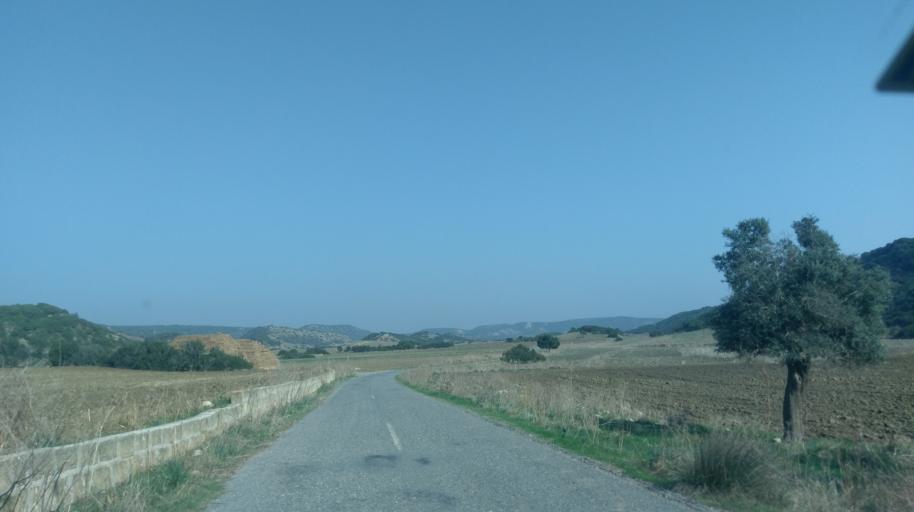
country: CY
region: Ammochostos
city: Rizokarpaso
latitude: 35.6375
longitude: 34.5116
